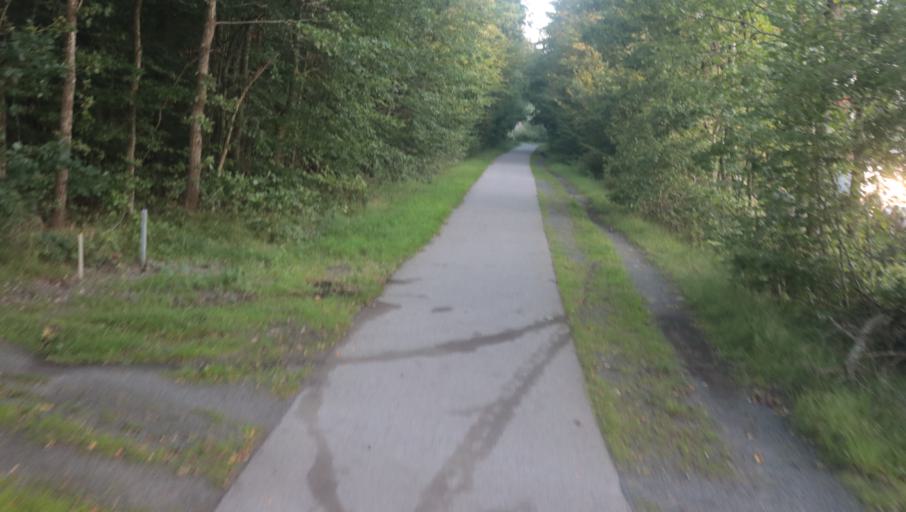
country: SE
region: Blekinge
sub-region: Karlshamns Kommun
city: Svangsta
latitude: 56.2252
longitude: 14.8170
